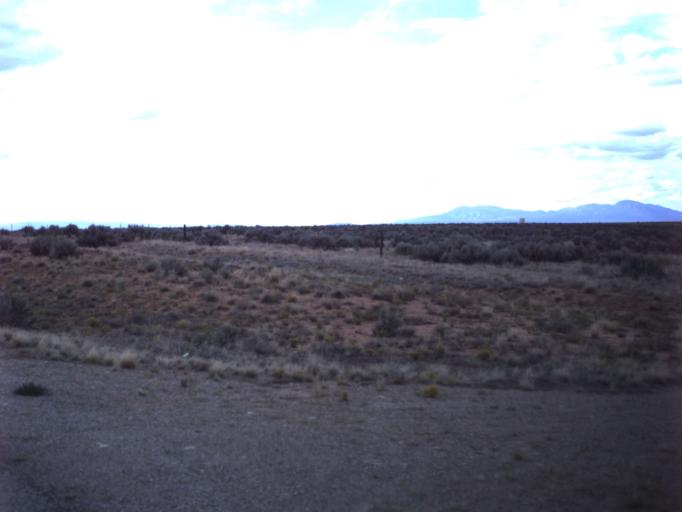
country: US
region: Utah
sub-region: San Juan County
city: Blanding
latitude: 37.4293
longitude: -109.3592
